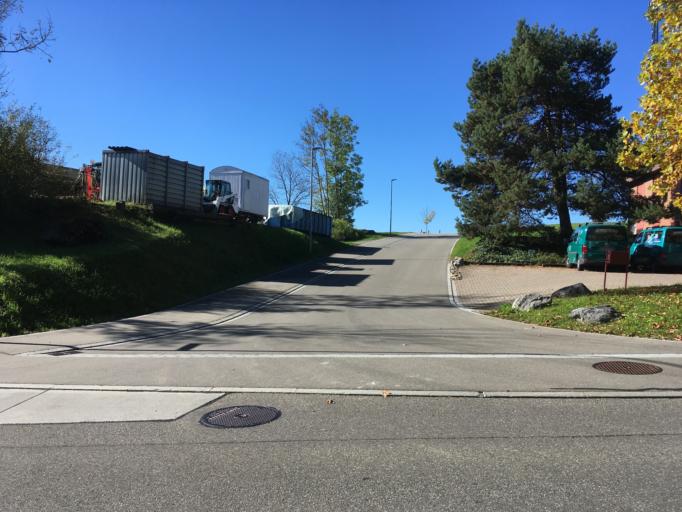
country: CH
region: Zurich
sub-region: Bezirk Hinwil
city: Baretswil
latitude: 47.3377
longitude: 8.8512
